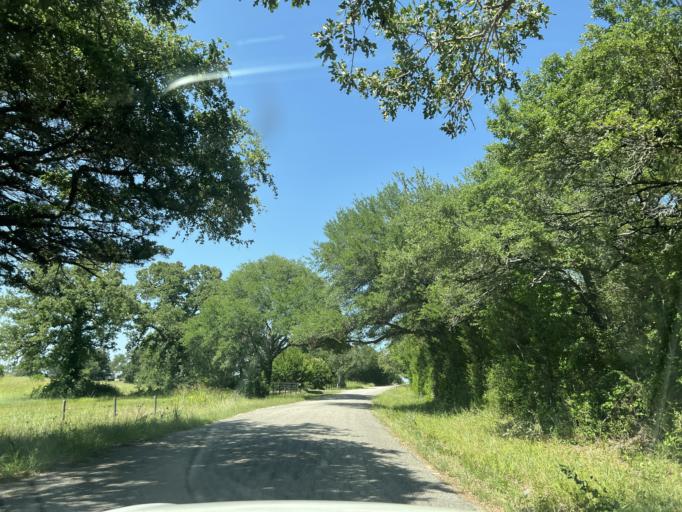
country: US
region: Texas
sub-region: Washington County
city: Brenham
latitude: 30.1636
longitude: -96.5221
